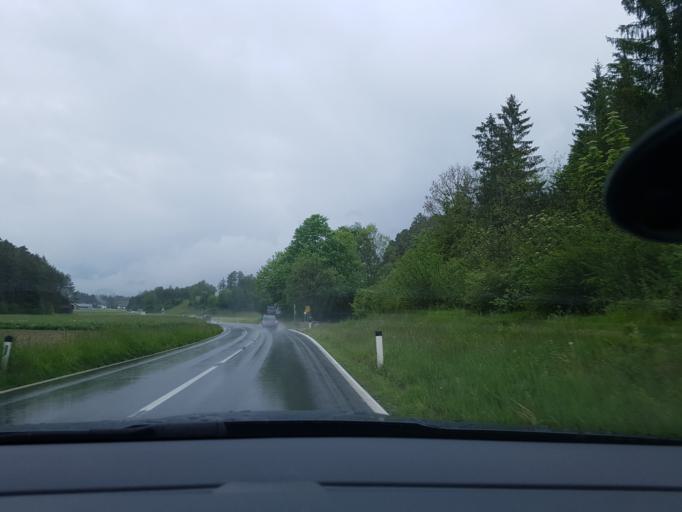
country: AT
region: Tyrol
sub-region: Politischer Bezirk Innsbruck Land
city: Wildermieming
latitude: 47.3123
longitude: 11.0185
